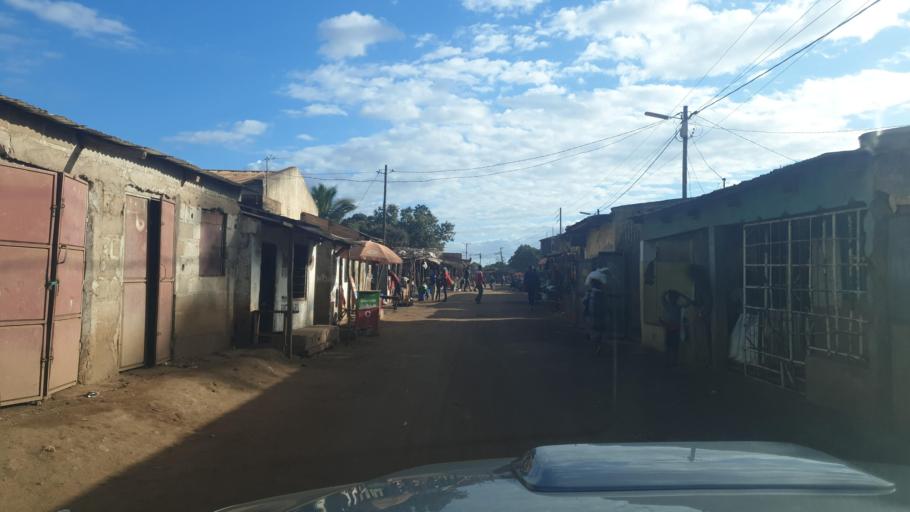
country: MZ
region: Nampula
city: Nampula
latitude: -15.1361
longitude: 39.2695
